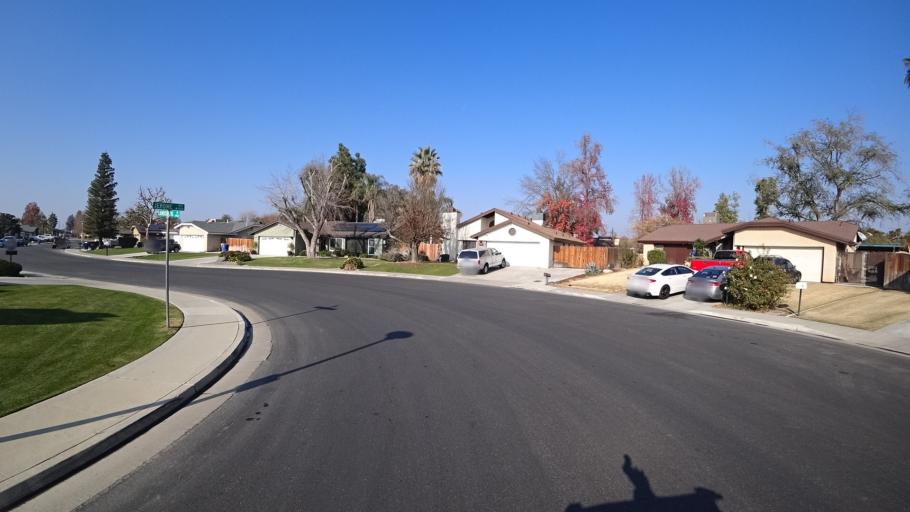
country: US
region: California
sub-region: Kern County
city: Greenacres
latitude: 35.3203
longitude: -119.0842
